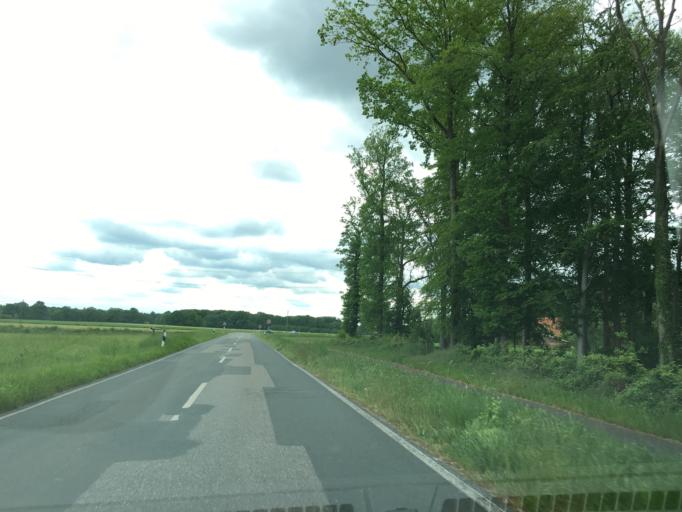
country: DE
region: North Rhine-Westphalia
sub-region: Regierungsbezirk Munster
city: Havixbeck
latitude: 51.9506
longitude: 7.5019
